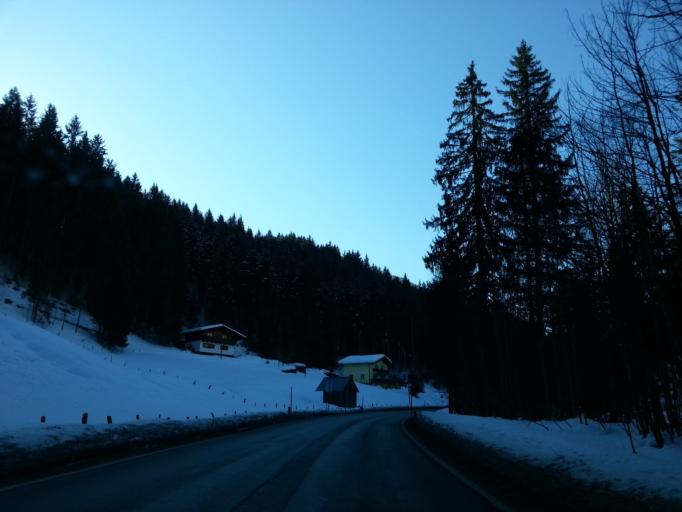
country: AT
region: Salzburg
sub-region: Politischer Bezirk Sankt Johann im Pongau
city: Eben im Pongau
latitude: 47.4896
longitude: 13.3967
